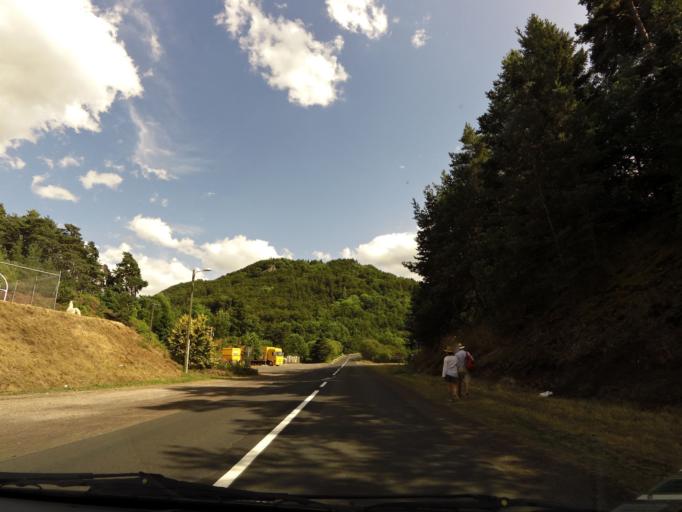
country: FR
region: Auvergne
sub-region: Departement du Puy-de-Dome
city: Aydat
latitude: 45.5692
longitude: 2.9469
